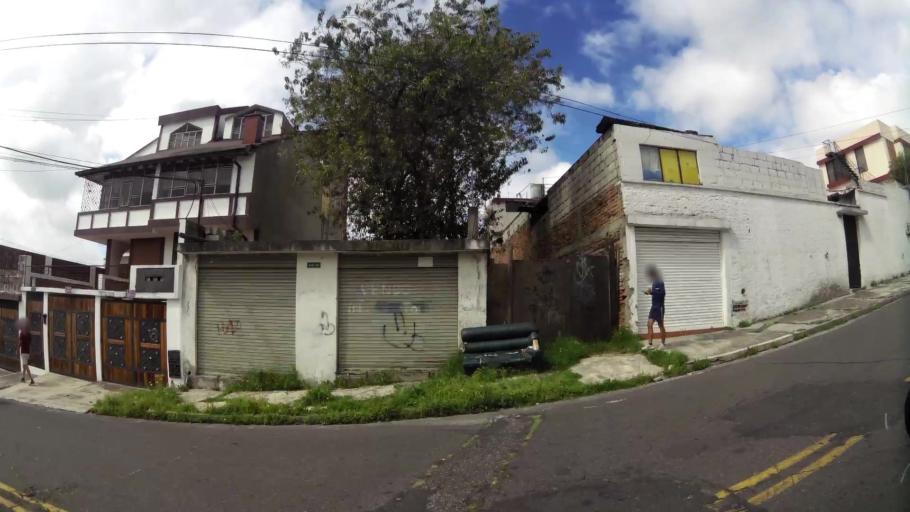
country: EC
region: Pichincha
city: Quito
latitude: -0.1467
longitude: -78.4968
